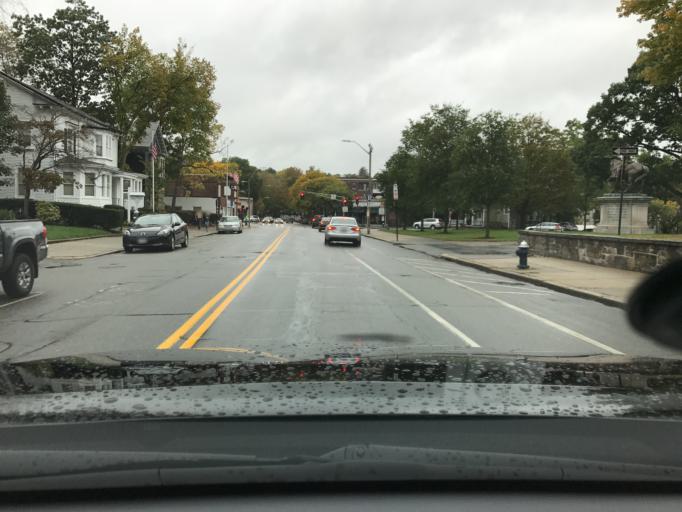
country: US
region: Massachusetts
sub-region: Norfolk County
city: Brookline
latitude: 42.3343
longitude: -71.1218
